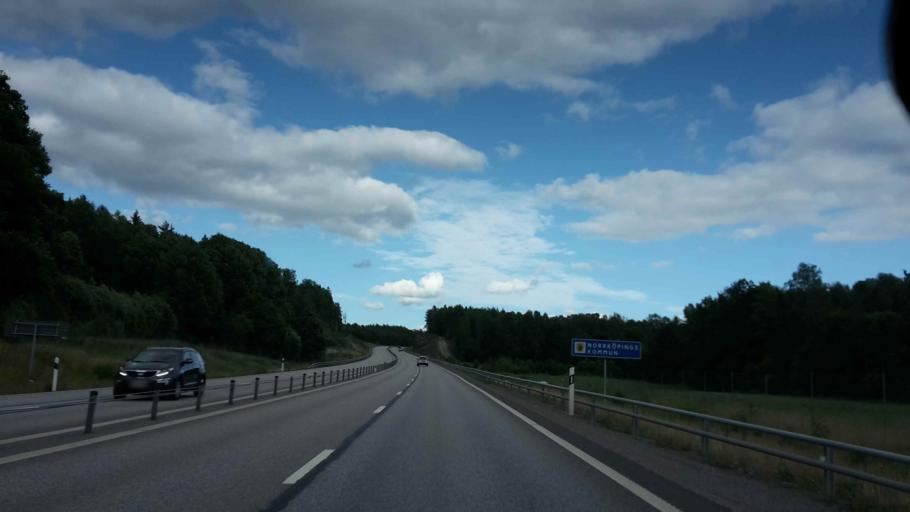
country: SE
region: OEstergoetland
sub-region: Norrkopings Kommun
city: Svartinge
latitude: 58.6708
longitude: 15.9760
